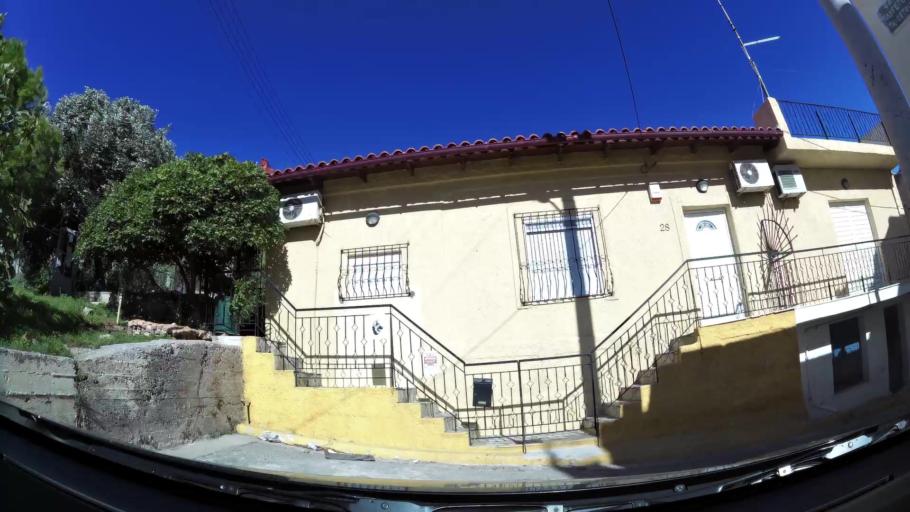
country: GR
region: Attica
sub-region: Nomos Piraios
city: Keratsini
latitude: 37.9657
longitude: 23.6069
